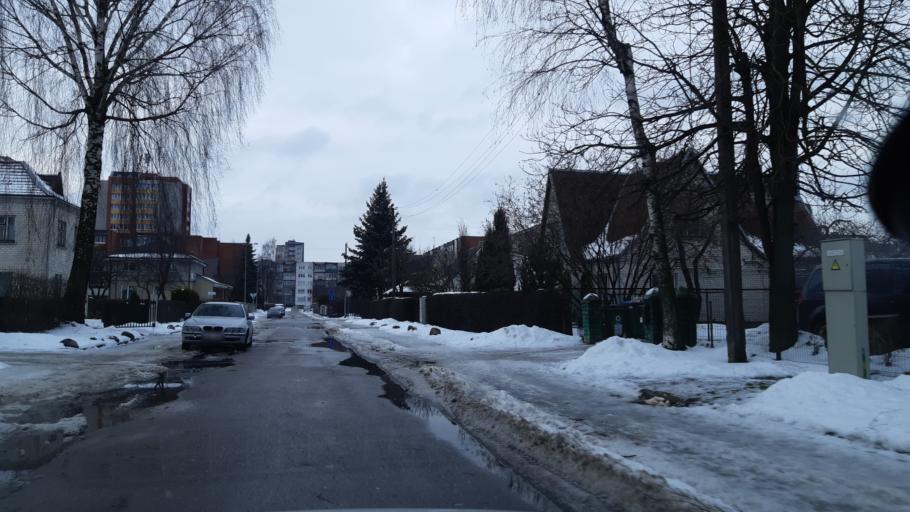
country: LT
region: Kauno apskritis
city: Dainava (Kaunas)
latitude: 54.9227
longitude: 23.9677
